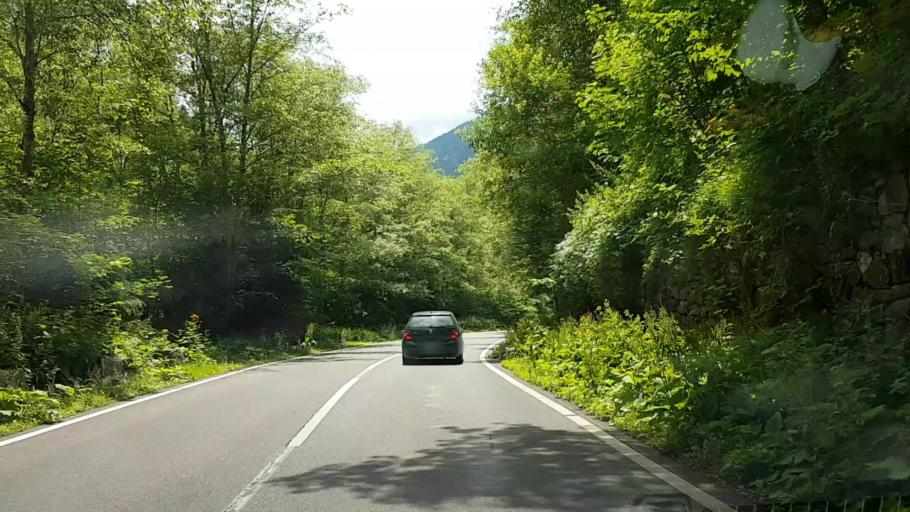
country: RO
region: Suceava
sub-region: Comuna Crucea
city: Crucea
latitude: 47.2965
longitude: 25.6323
